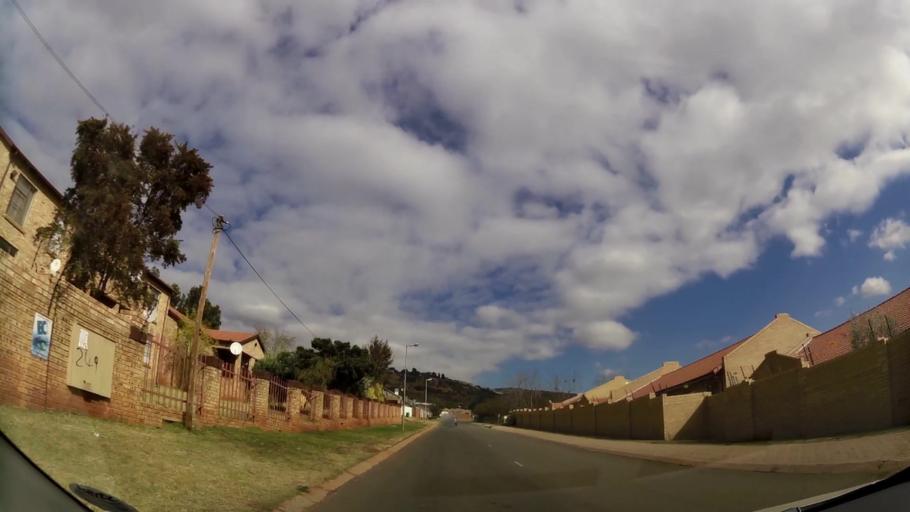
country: ZA
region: Gauteng
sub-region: City of Johannesburg Metropolitan Municipality
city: Roodepoort
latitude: -26.1032
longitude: 27.8731
